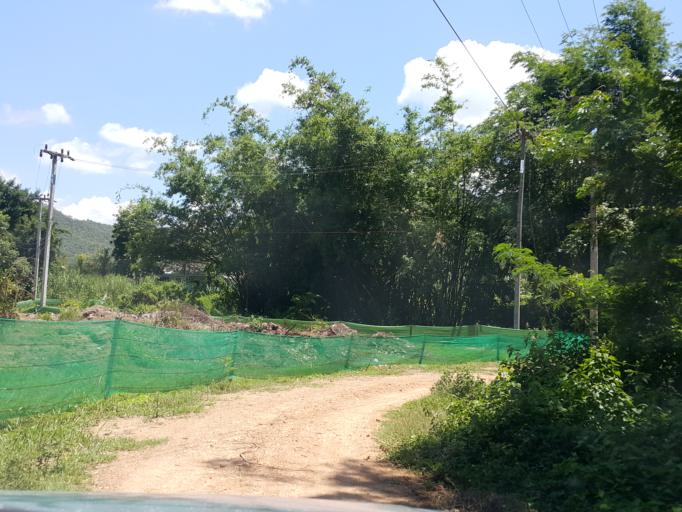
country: TH
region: Lamphun
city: Ban Thi
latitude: 18.6833
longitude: 99.1695
